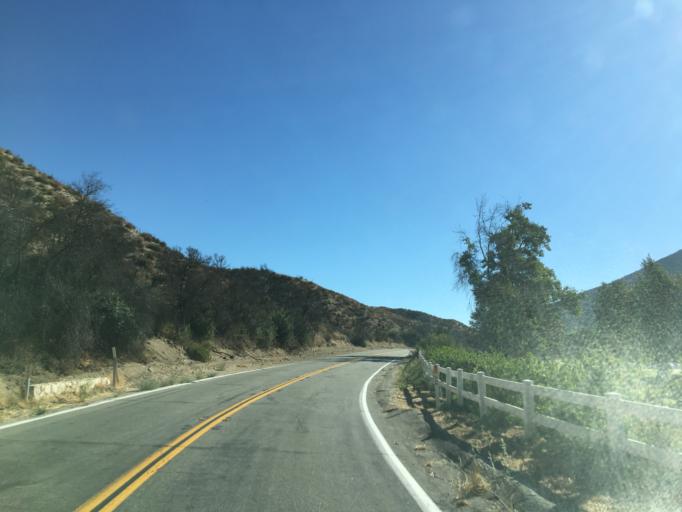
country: US
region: California
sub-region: Los Angeles County
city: Green Valley
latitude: 34.6408
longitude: -118.5008
